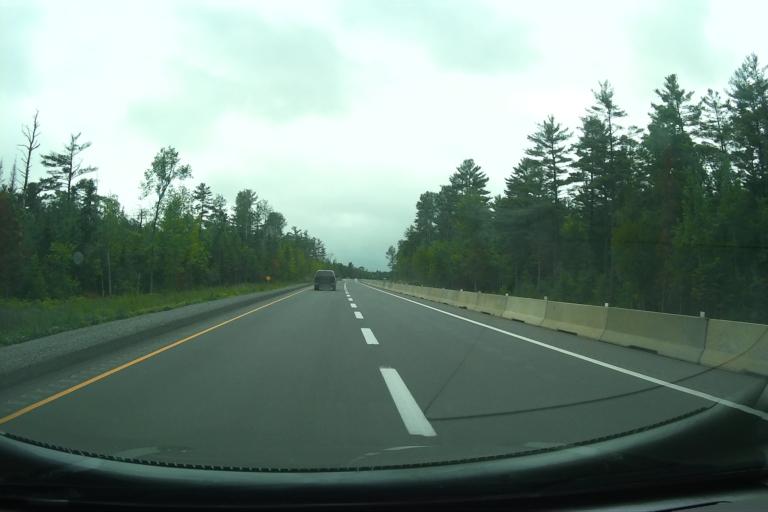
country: CA
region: Ontario
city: Arnprior
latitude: 45.4377
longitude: -76.4496
